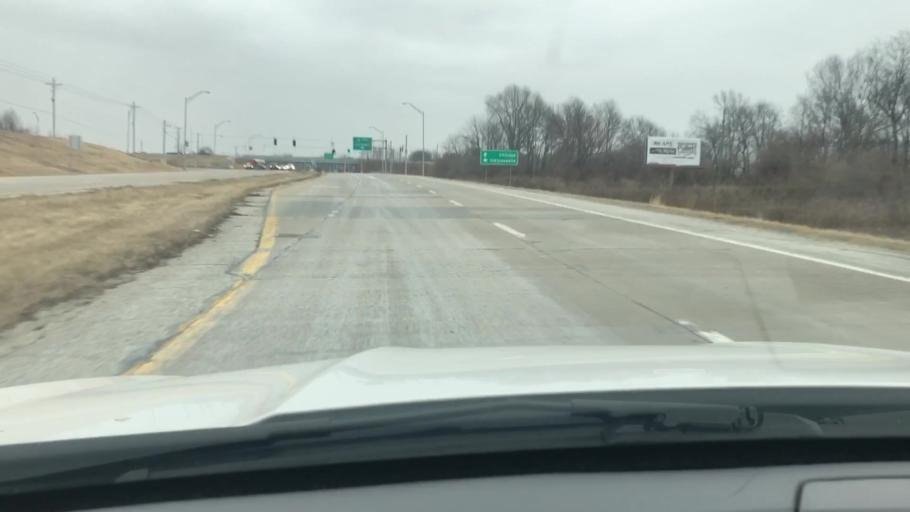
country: US
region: Indiana
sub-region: Tippecanoe County
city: Dayton
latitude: 40.3739
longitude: -86.7890
